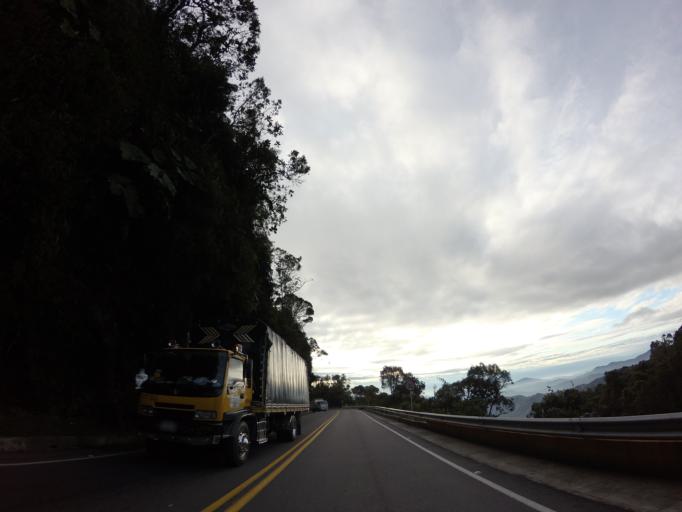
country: CO
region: Tolima
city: Herveo
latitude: 5.0947
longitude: -75.2781
